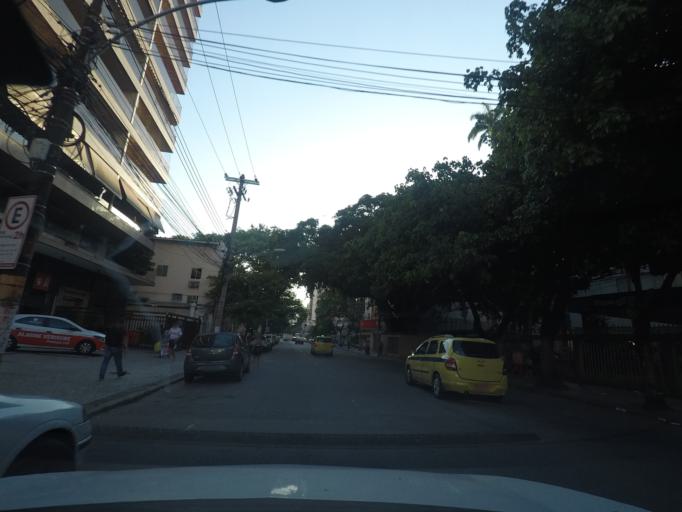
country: BR
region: Rio de Janeiro
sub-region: Rio De Janeiro
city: Rio de Janeiro
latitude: -22.9152
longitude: -43.2207
